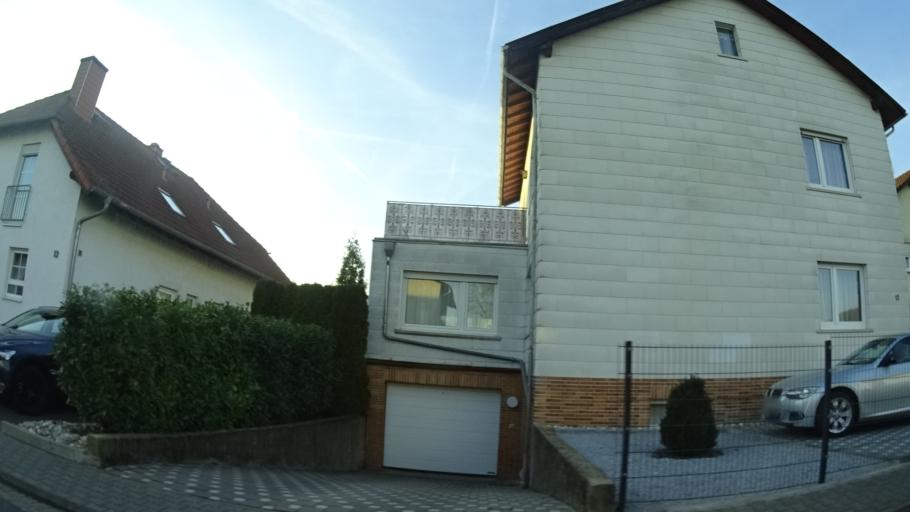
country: DE
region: Hesse
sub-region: Regierungsbezirk Darmstadt
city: Gelnhausen
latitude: 50.1878
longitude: 9.2022
